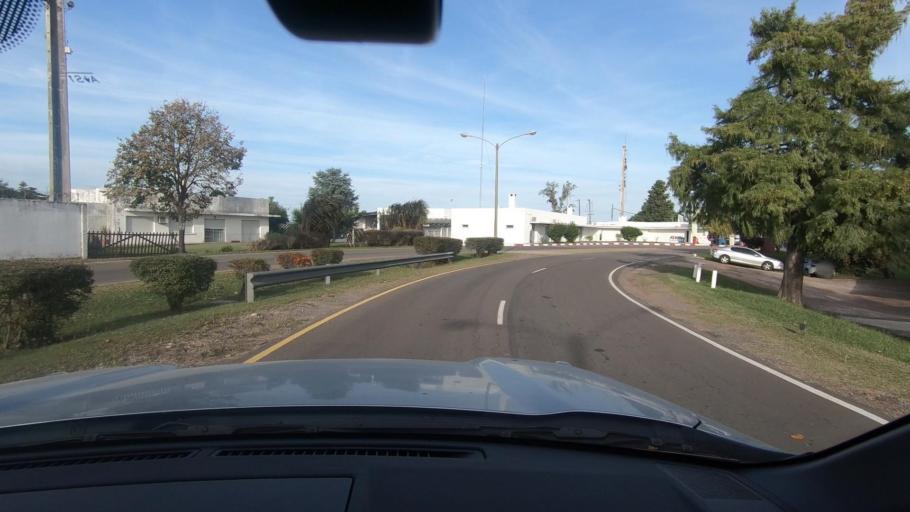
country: AR
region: Entre Rios
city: Colon
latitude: -32.2470
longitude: -58.1445
